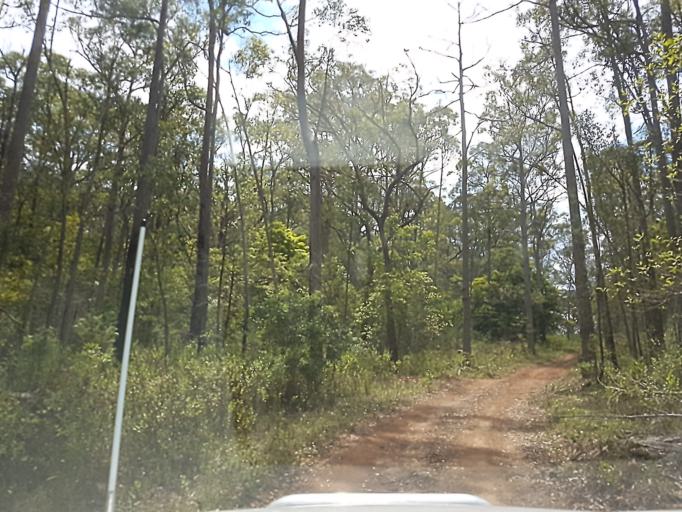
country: AU
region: Victoria
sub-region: East Gippsland
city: Lakes Entrance
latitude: -37.3493
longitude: 148.3572
